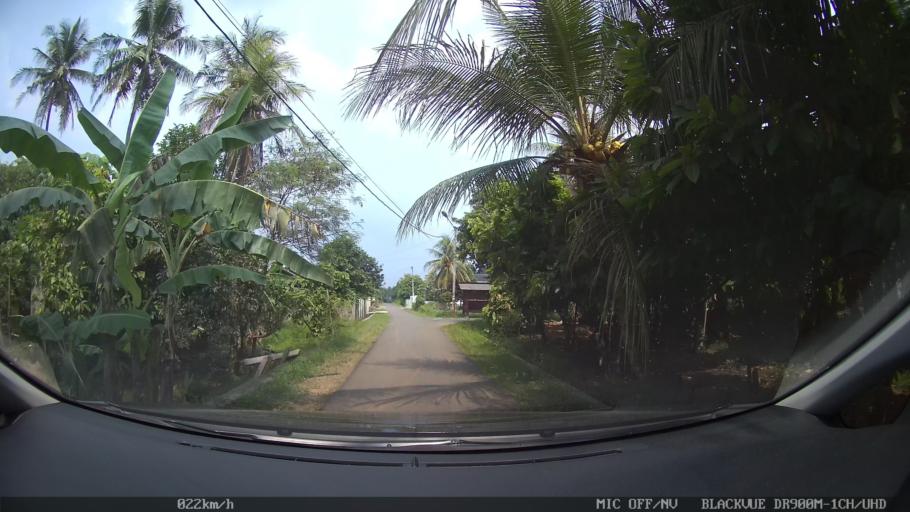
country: ID
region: Lampung
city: Gadingrejo
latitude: -5.3652
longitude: 105.0627
